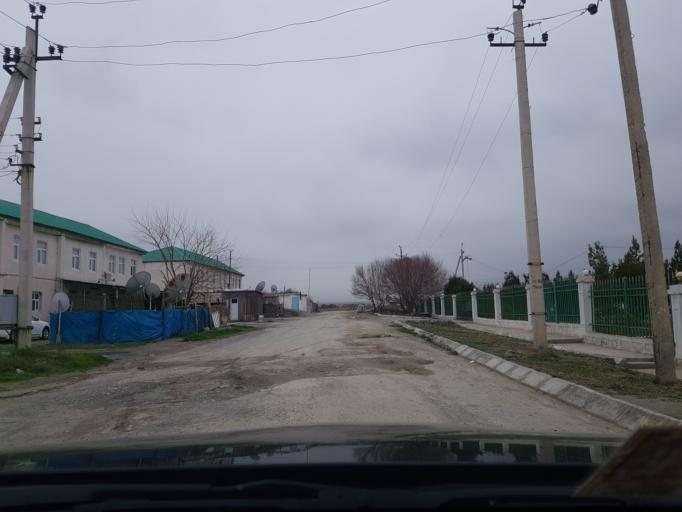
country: TM
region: Ahal
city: Abadan
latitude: 38.1620
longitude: 57.9431
